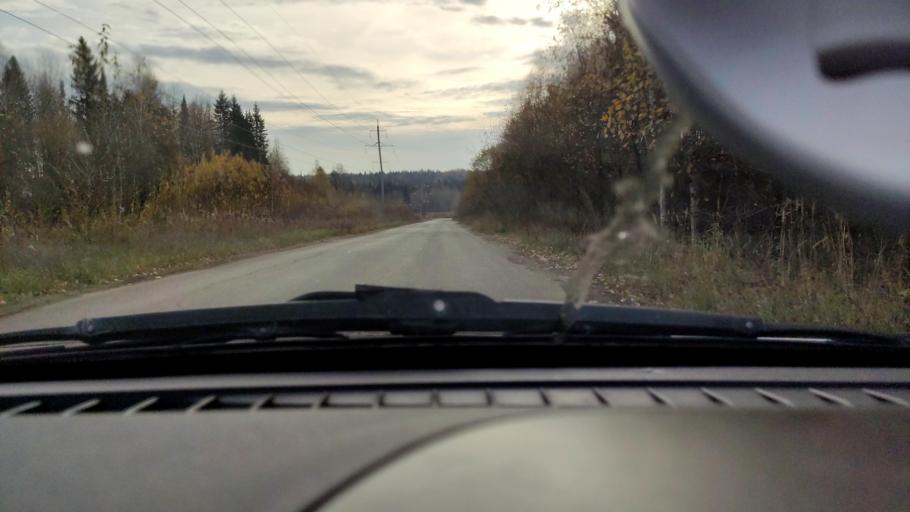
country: RU
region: Perm
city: Perm
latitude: 58.0898
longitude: 56.4155
